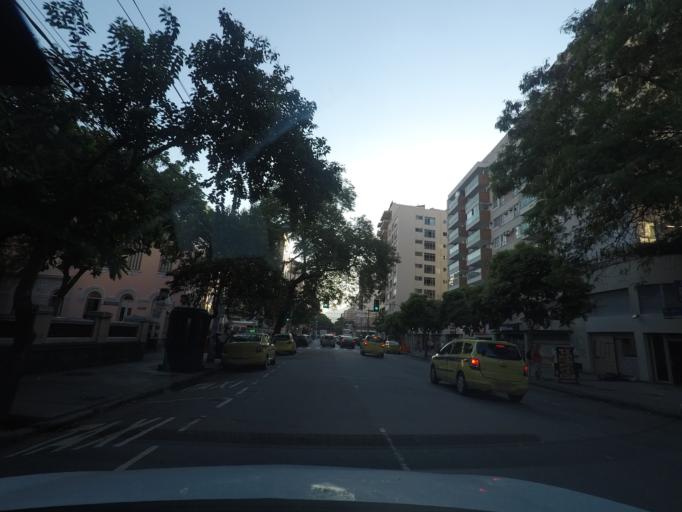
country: BR
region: Rio de Janeiro
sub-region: Rio De Janeiro
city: Rio de Janeiro
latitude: -22.9157
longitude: -43.2212
